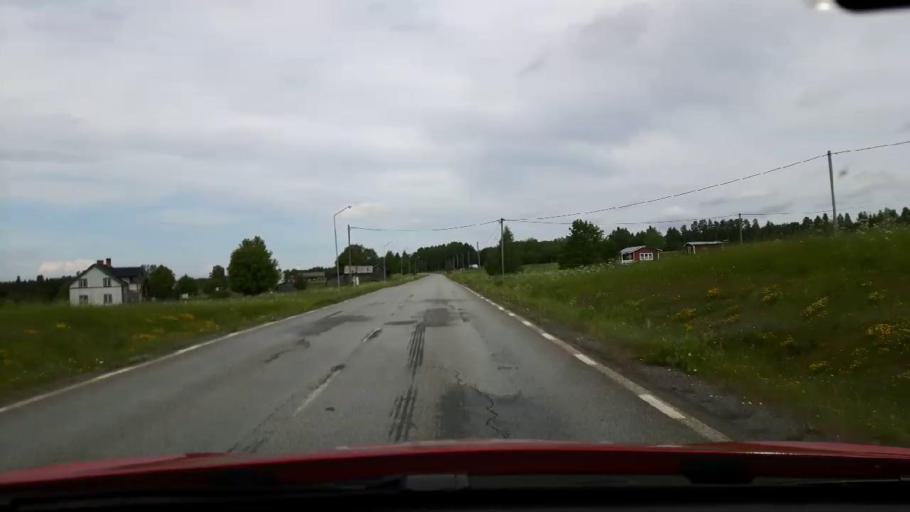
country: SE
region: Jaemtland
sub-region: Bergs Kommun
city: Hoverberg
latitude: 63.0133
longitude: 14.4918
